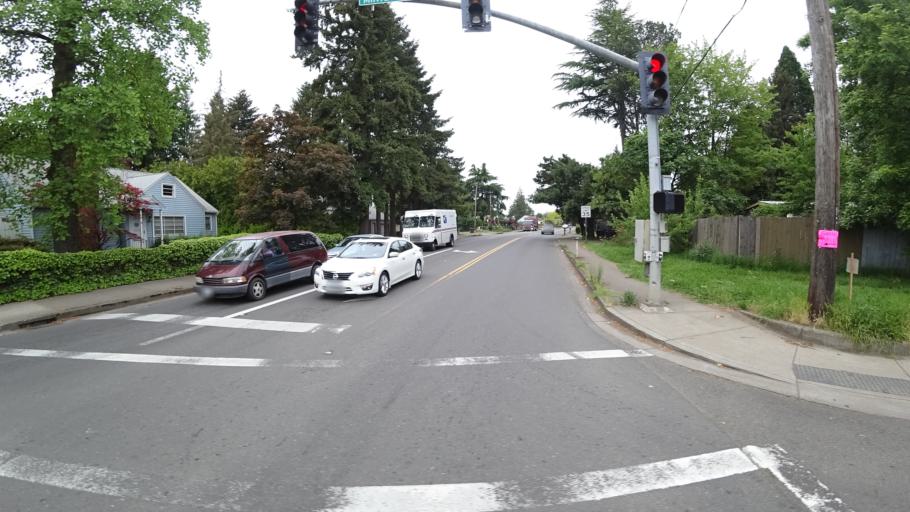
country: US
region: Oregon
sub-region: Washington County
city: Hillsboro
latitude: 45.5045
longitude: -122.9629
